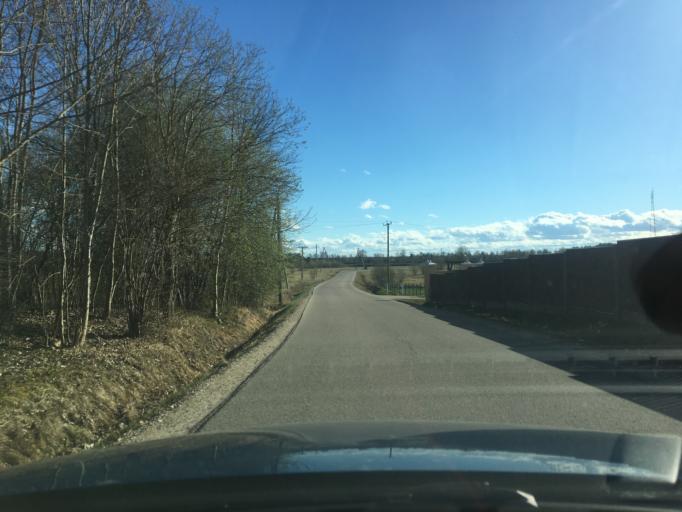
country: LV
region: Salaspils
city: Salaspils
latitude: 56.8702
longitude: 24.3235
